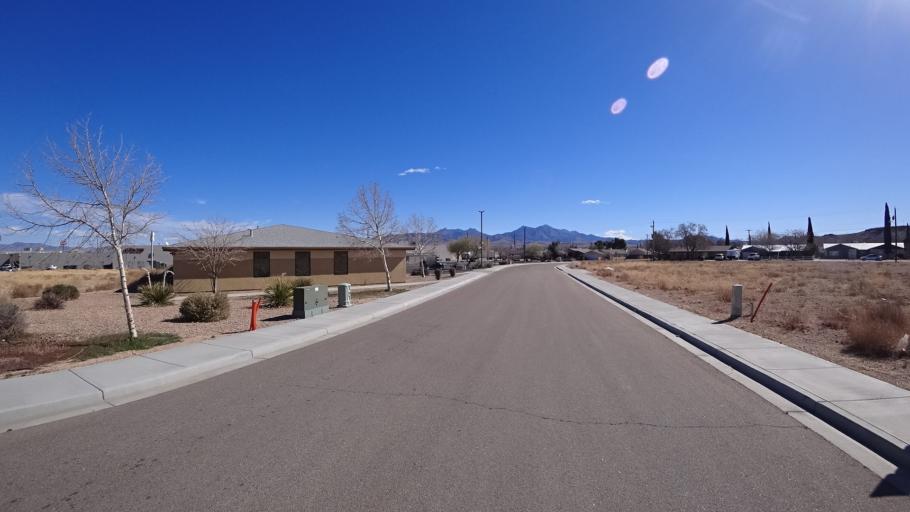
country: US
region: Arizona
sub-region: Mohave County
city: Kingman
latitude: 35.2149
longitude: -114.0386
